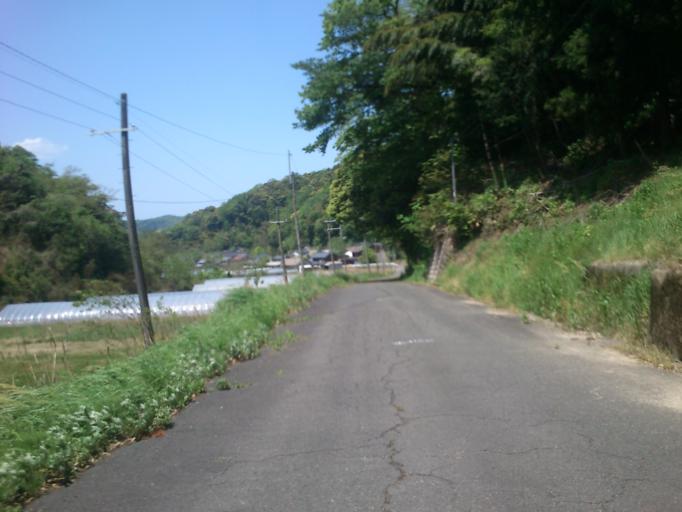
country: JP
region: Kyoto
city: Miyazu
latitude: 35.7153
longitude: 135.1255
